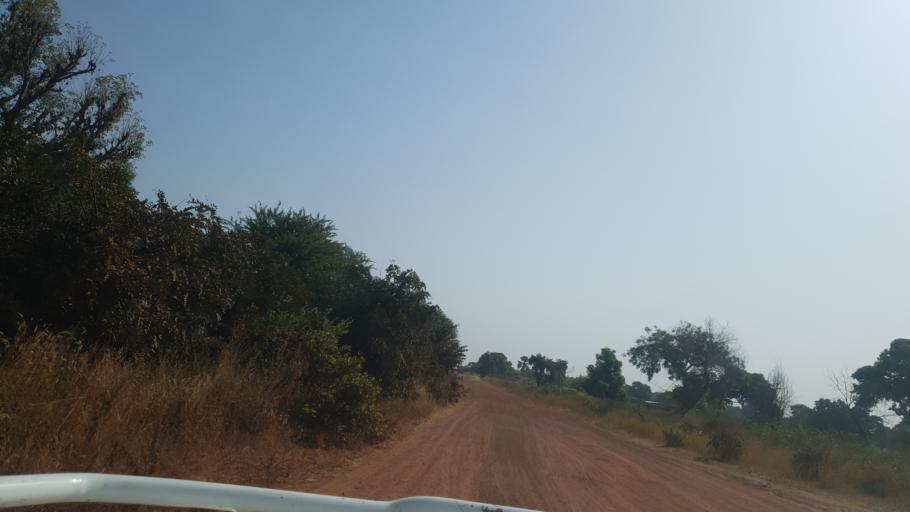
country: ML
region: Koulikoro
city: Dioila
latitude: 12.6687
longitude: -6.6781
